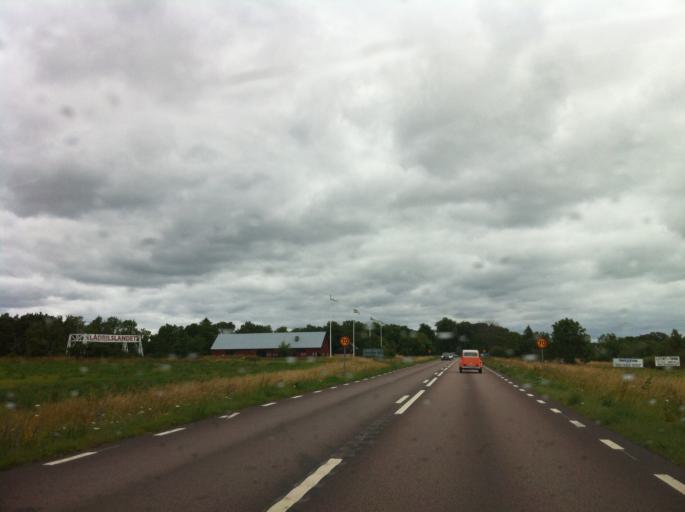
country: SE
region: Kalmar
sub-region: Borgholms Kommun
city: Borgholm
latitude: 57.1561
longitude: 17.0097
